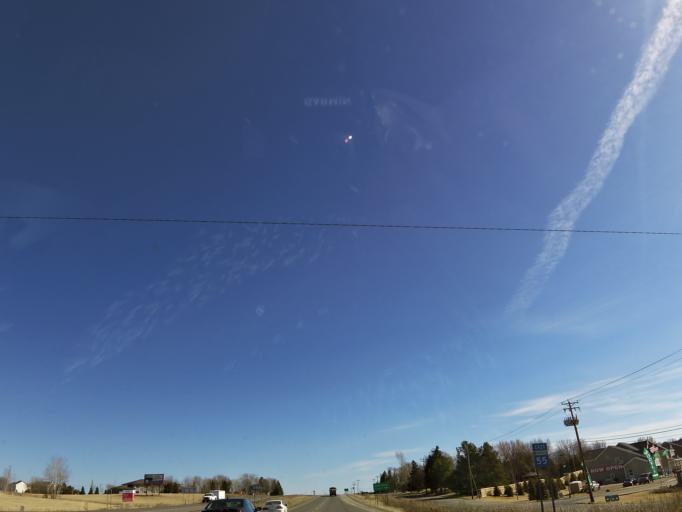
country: US
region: Minnesota
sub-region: Hennepin County
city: Wayzata
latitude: 45.0378
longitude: -93.5160
